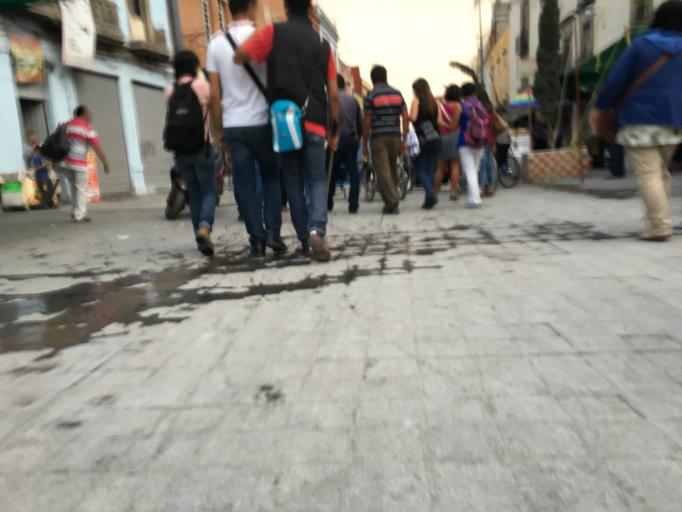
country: MX
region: Mexico City
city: Mexico City
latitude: 19.4309
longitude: -99.1270
